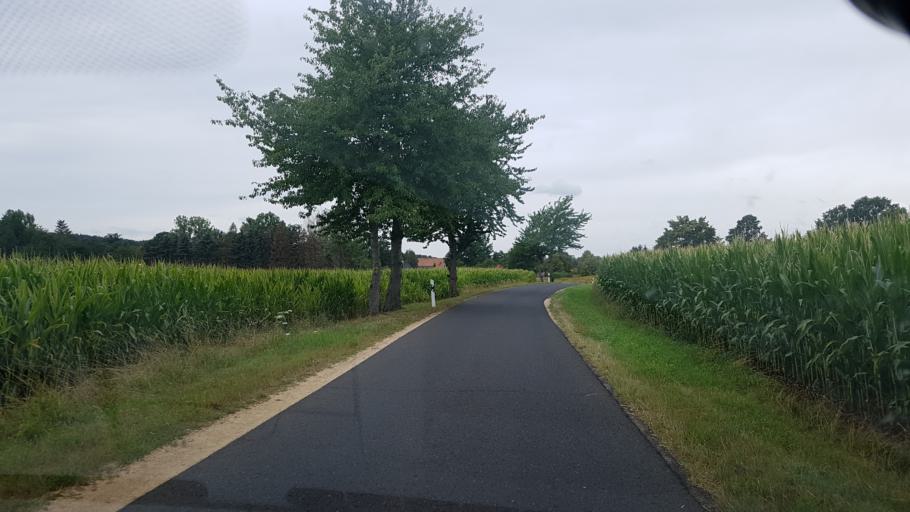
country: DE
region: Saxony
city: Kodersdorf
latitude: 51.2257
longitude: 14.8664
